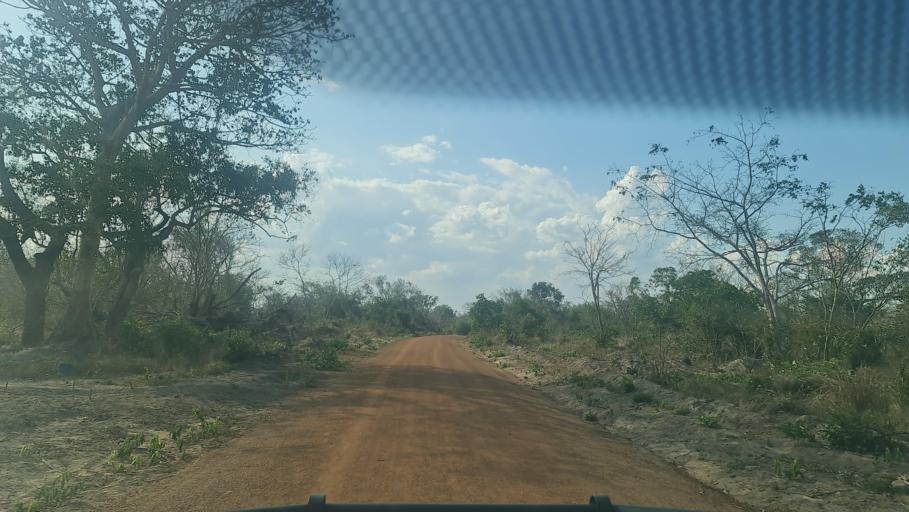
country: MZ
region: Nampula
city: Ilha de Mocambique
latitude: -15.5040
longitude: 40.1627
